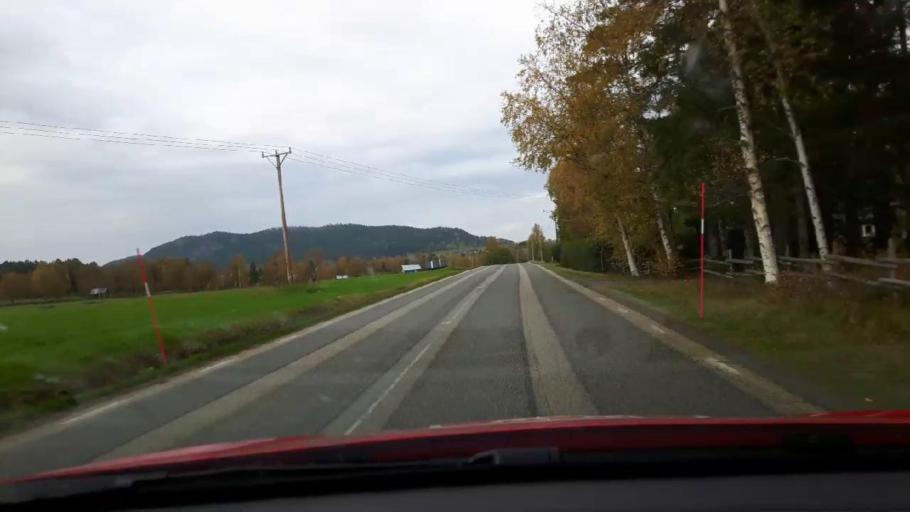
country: SE
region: Jaemtland
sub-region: Bergs Kommun
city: Hoverberg
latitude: 62.7954
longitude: 14.4377
